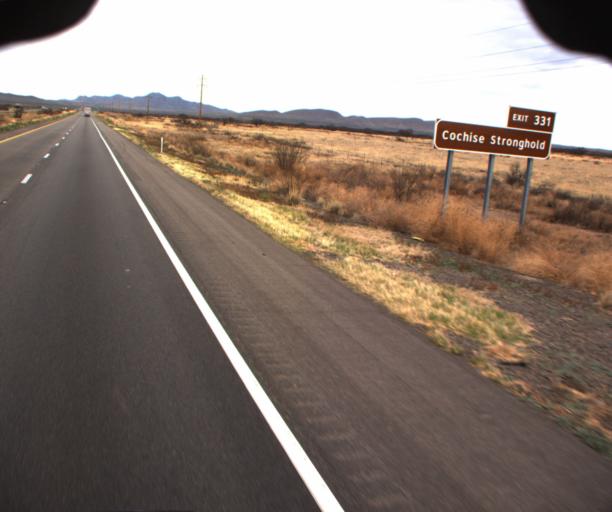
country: US
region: Arizona
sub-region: Cochise County
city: Willcox
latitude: 32.1927
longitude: -109.9225
